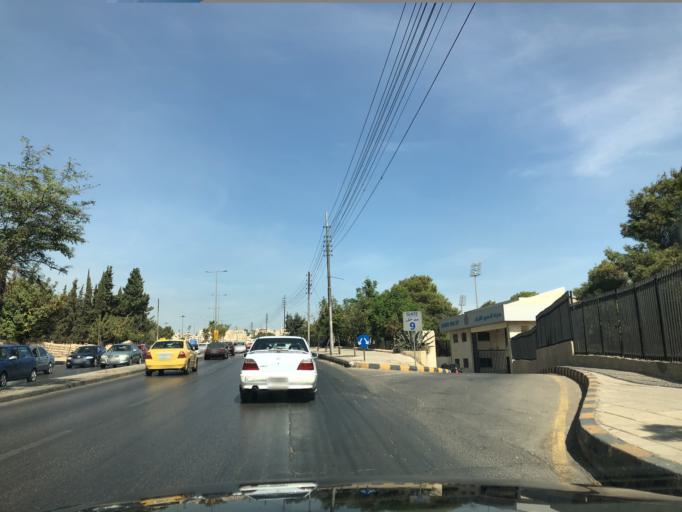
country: JO
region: Amman
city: Amman
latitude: 31.9809
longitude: 35.9022
